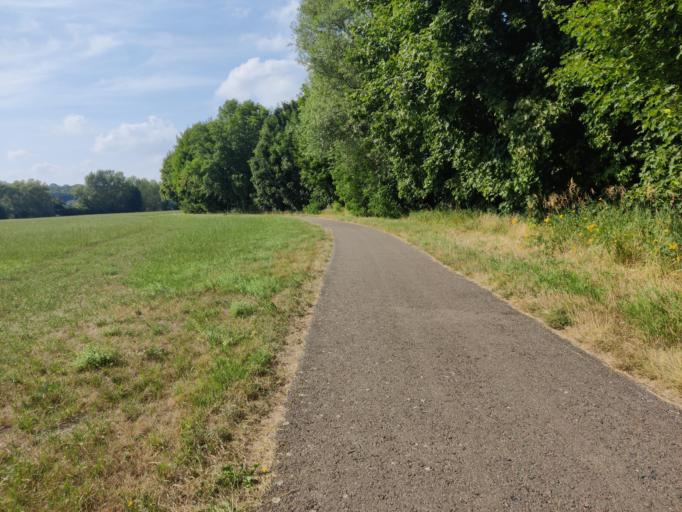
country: DE
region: Thuringia
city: Haselbach
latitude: 51.0596
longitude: 12.4498
